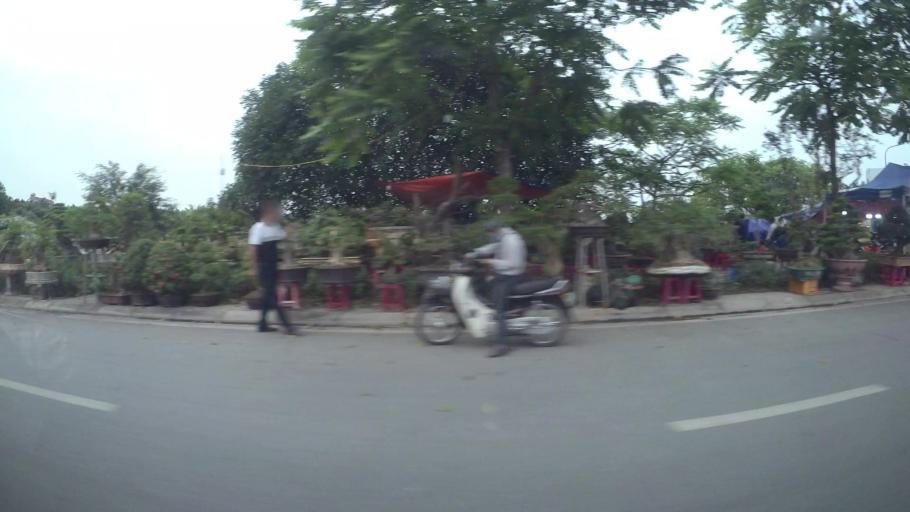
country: VN
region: Ha Noi
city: Hoan Kiem
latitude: 21.0538
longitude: 105.8929
